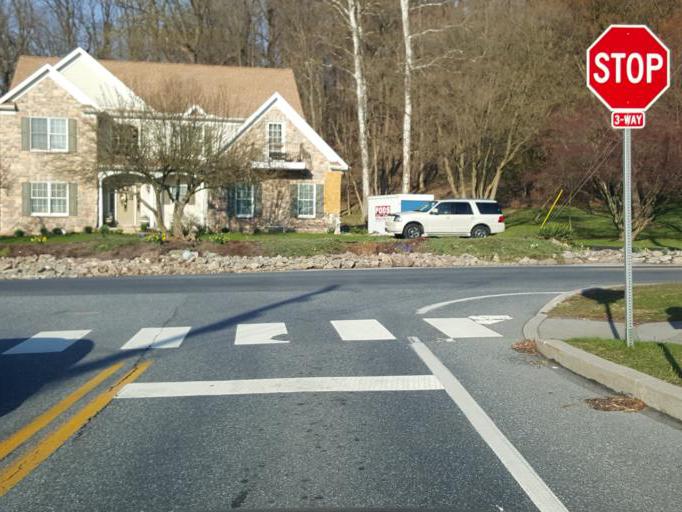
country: US
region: Pennsylvania
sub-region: Dauphin County
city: Hummelstown
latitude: 40.2584
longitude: -76.6850
